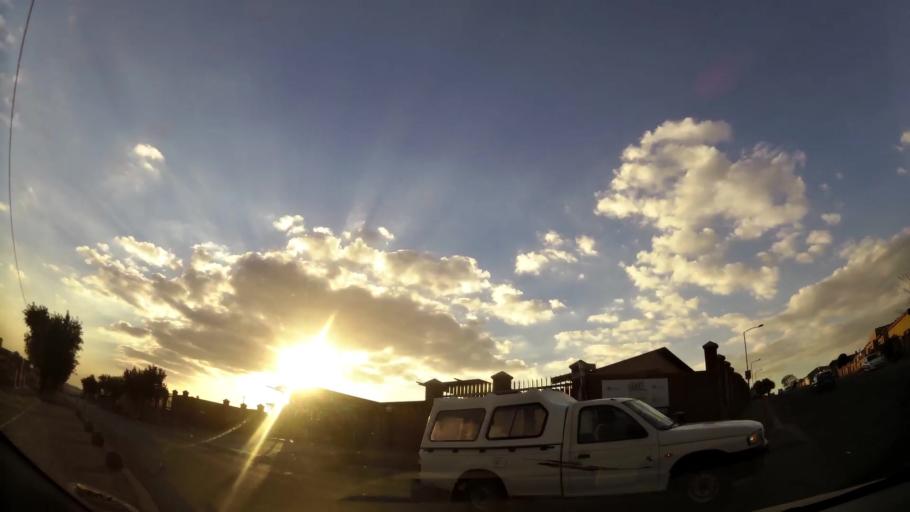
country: ZA
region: Gauteng
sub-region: West Rand District Municipality
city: Krugersdorp
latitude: -26.0811
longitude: 27.7529
